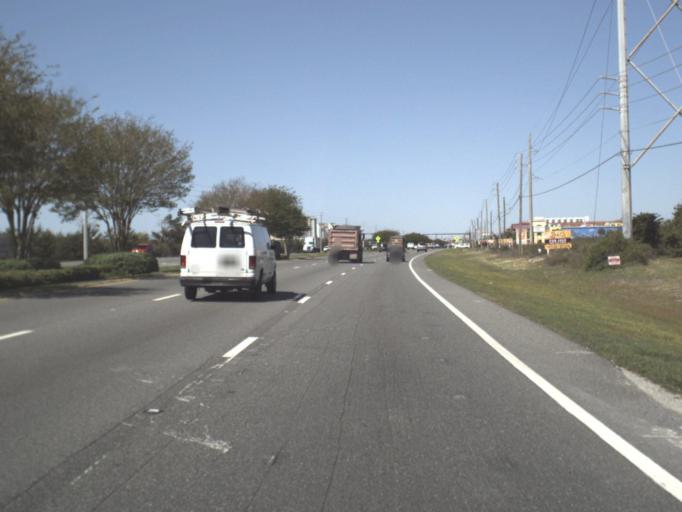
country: US
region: Florida
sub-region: Okaloosa County
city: Destin
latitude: 30.3870
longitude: -86.4393
